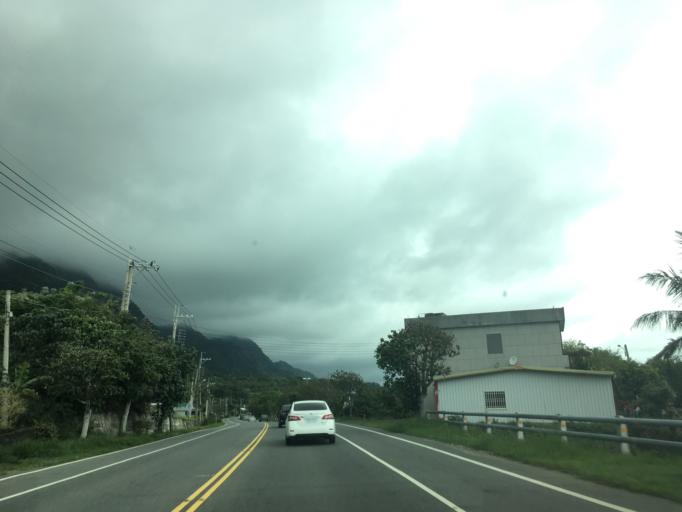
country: TW
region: Taiwan
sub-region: Taitung
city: Taitung
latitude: 23.0090
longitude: 121.3237
